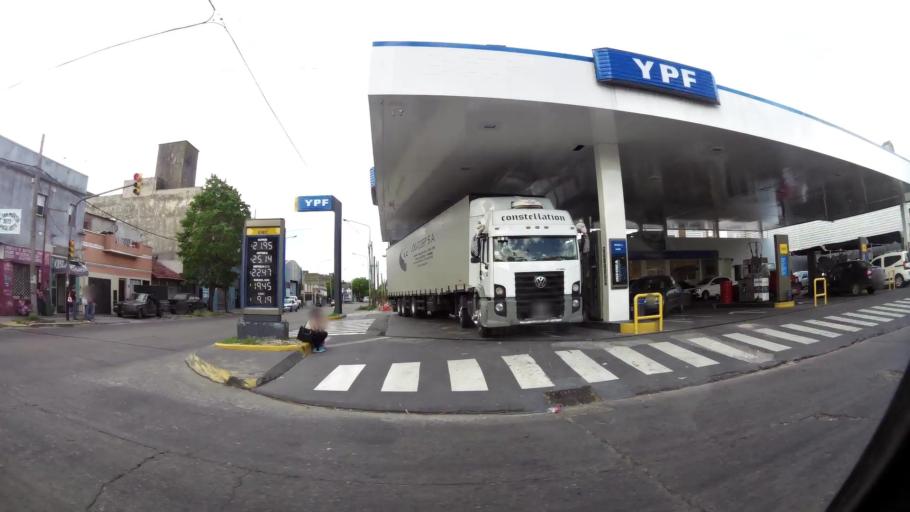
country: AR
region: Buenos Aires
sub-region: Partido de Lanus
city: Lanus
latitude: -34.6977
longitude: -58.3700
